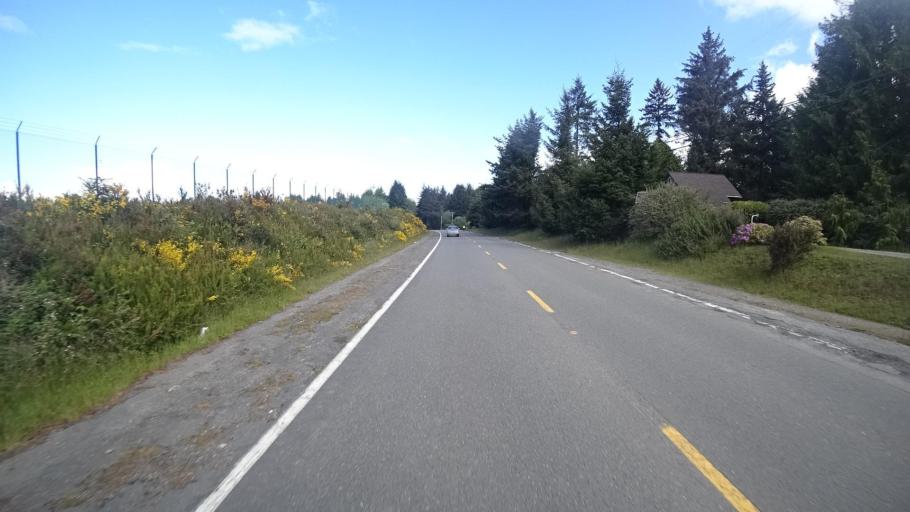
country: US
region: California
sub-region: Humboldt County
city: McKinleyville
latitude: 40.9825
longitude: -124.1027
